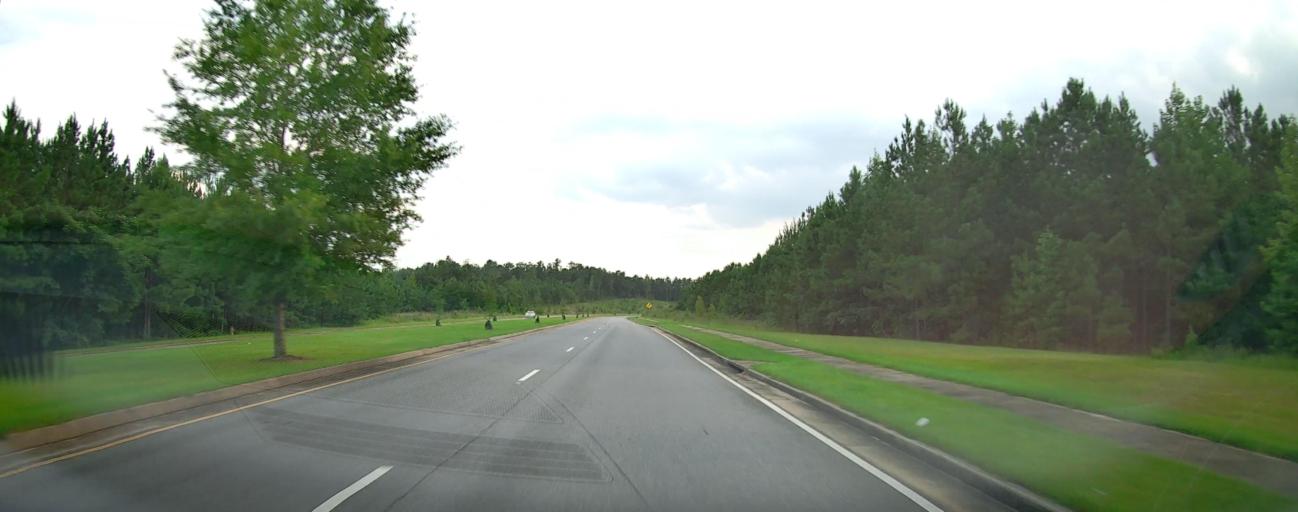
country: US
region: Georgia
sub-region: Muscogee County
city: Columbus
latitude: 32.5171
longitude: -84.8451
